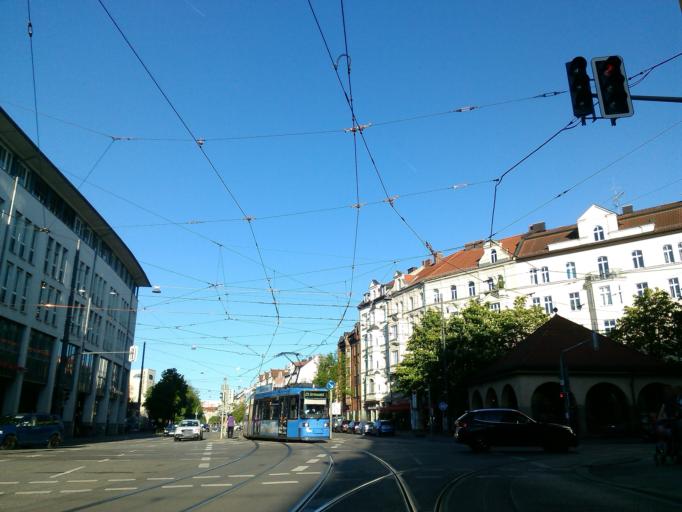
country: DE
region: Bavaria
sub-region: Upper Bavaria
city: Munich
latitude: 48.1358
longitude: 11.5976
